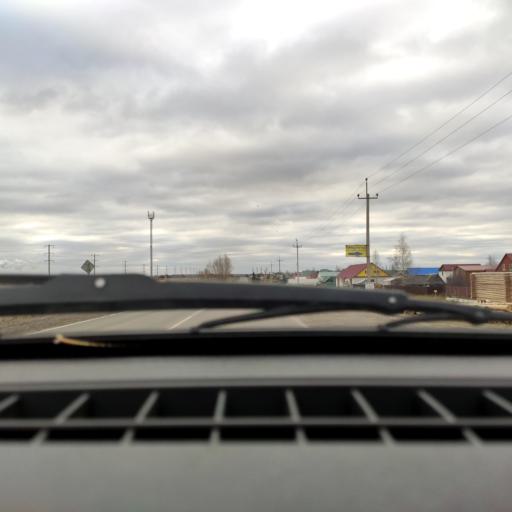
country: RU
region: Bashkortostan
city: Iglino
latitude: 54.7871
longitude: 56.2523
